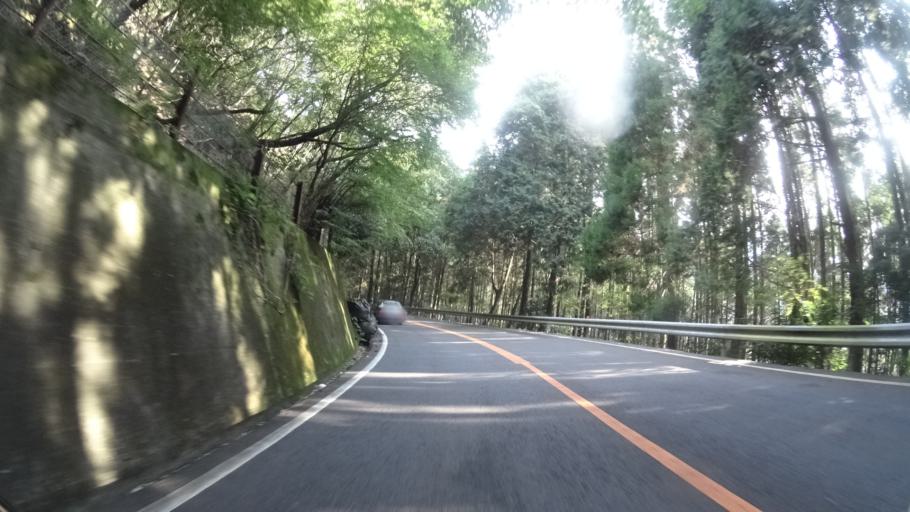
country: JP
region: Oita
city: Beppu
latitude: 33.2657
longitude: 131.3709
